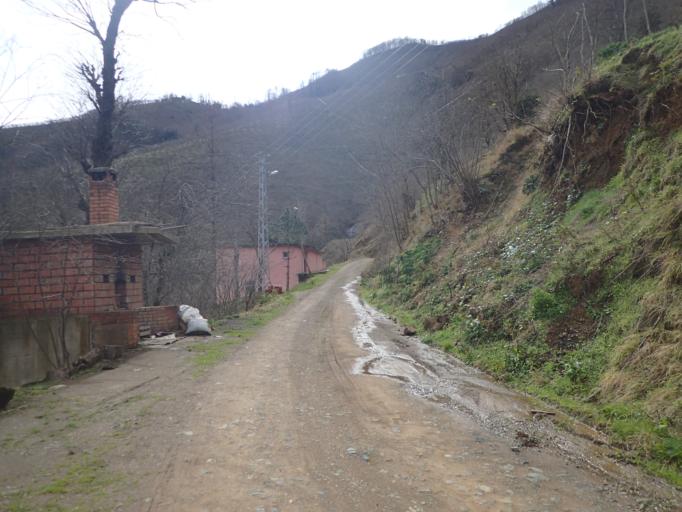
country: TR
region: Ordu
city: Camas
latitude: 40.8963
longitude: 37.5783
